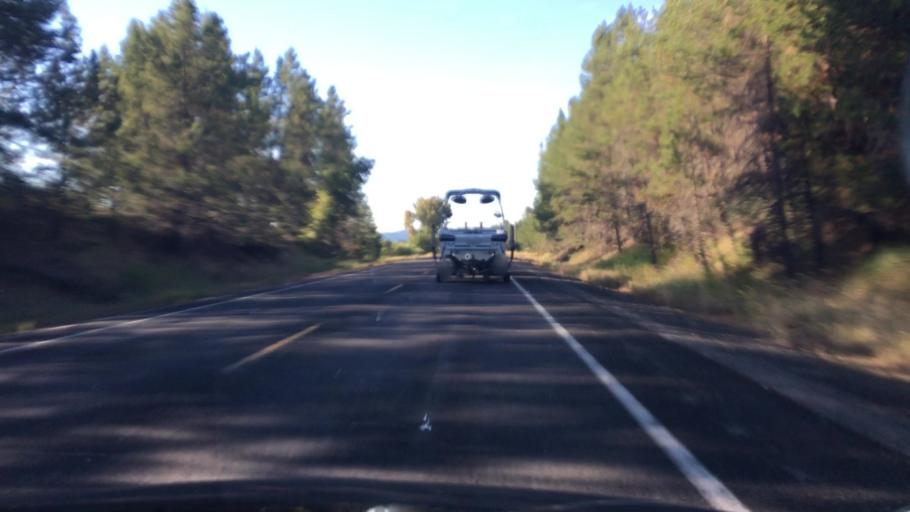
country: US
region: Idaho
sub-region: Valley County
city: Cascade
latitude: 44.4649
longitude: -115.9992
